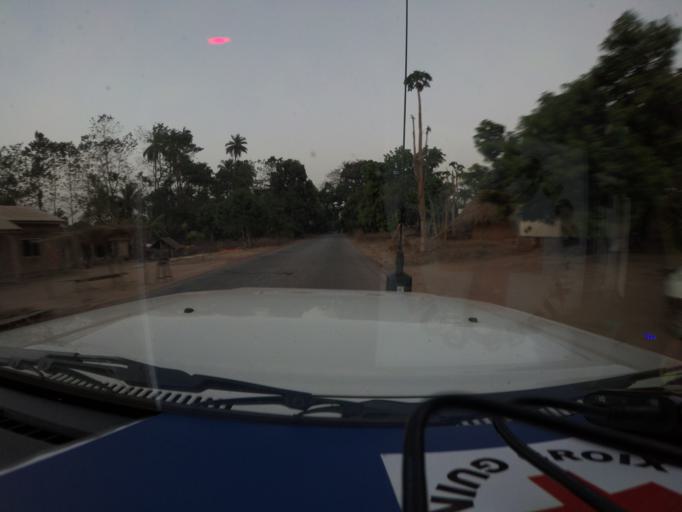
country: GN
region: Kindia
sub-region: Kindia
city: Kindia
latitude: 9.9287
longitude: -12.9900
